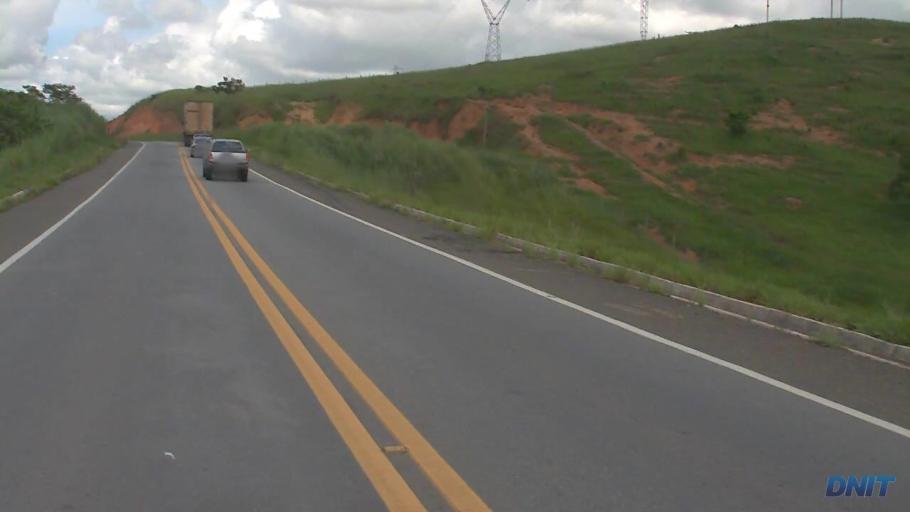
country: BR
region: Minas Gerais
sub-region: Belo Oriente
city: Belo Oriente
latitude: -19.0998
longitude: -42.1982
